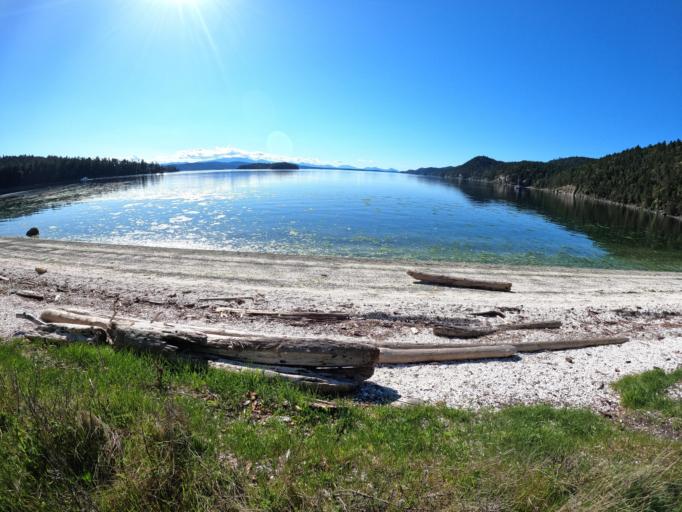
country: CA
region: British Columbia
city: North Saanich
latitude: 48.8981
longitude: -123.4082
